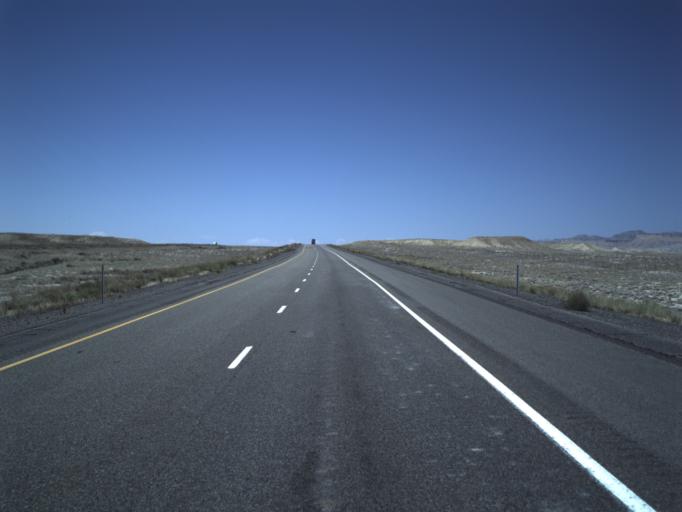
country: US
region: Utah
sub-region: Grand County
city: Moab
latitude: 38.9427
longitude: -109.5311
